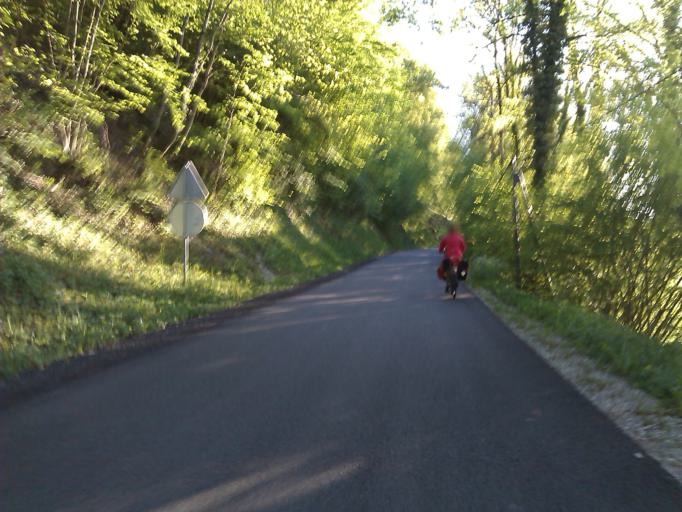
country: FR
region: Franche-Comte
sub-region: Departement du Doubs
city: Clerval
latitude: 47.3682
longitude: 6.4903
